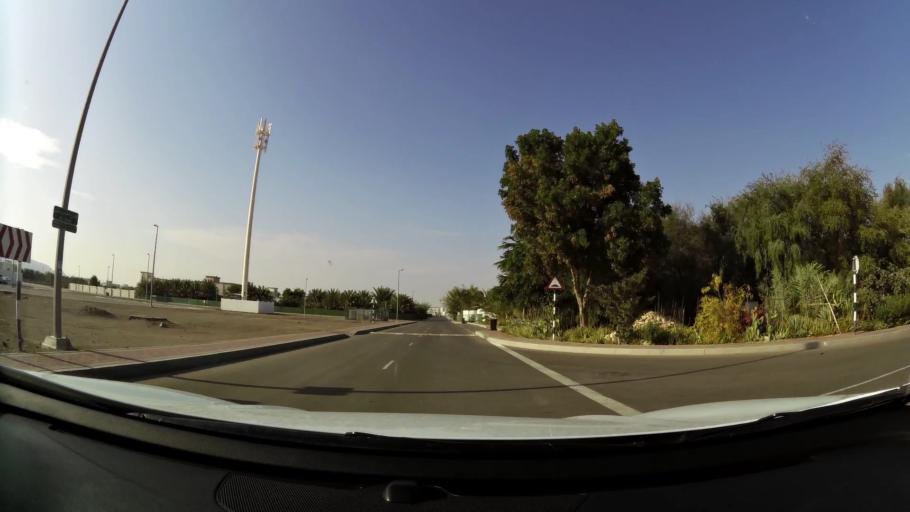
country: AE
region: Abu Dhabi
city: Al Ain
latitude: 24.0613
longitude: 55.8493
